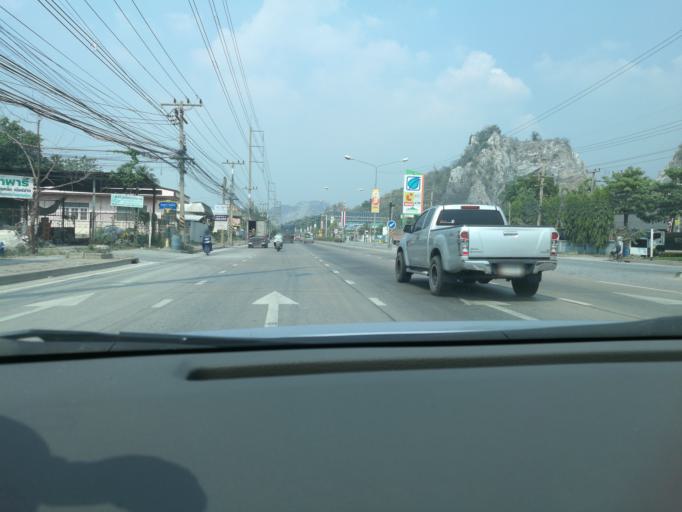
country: TH
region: Sara Buri
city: Phra Phutthabat
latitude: 14.6930
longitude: 100.8679
